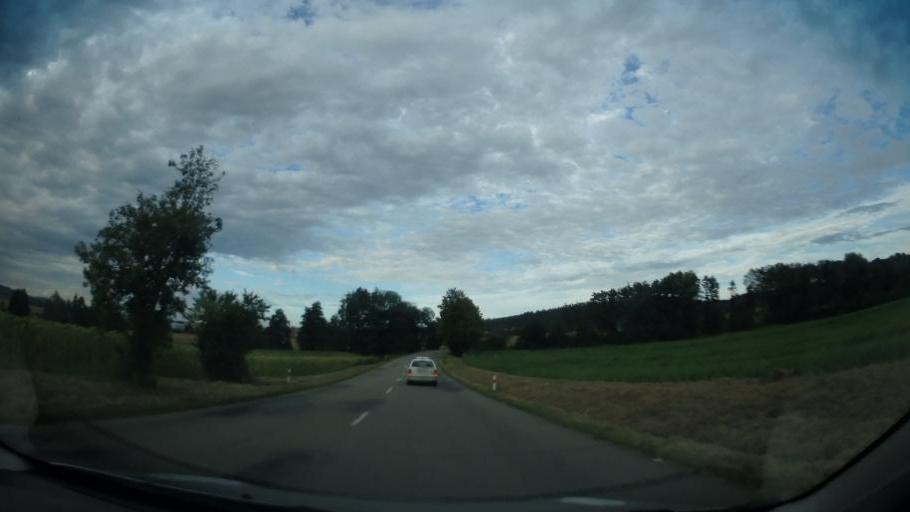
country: CZ
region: South Moravian
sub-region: Okres Blansko
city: Boskovice
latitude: 49.5424
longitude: 16.7036
